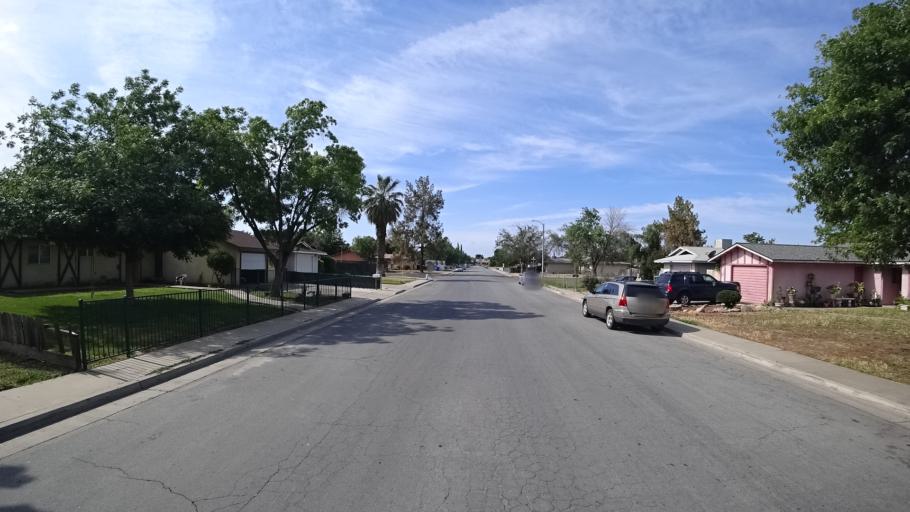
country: US
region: California
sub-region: Kings County
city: Hanford
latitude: 36.3124
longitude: -119.6599
